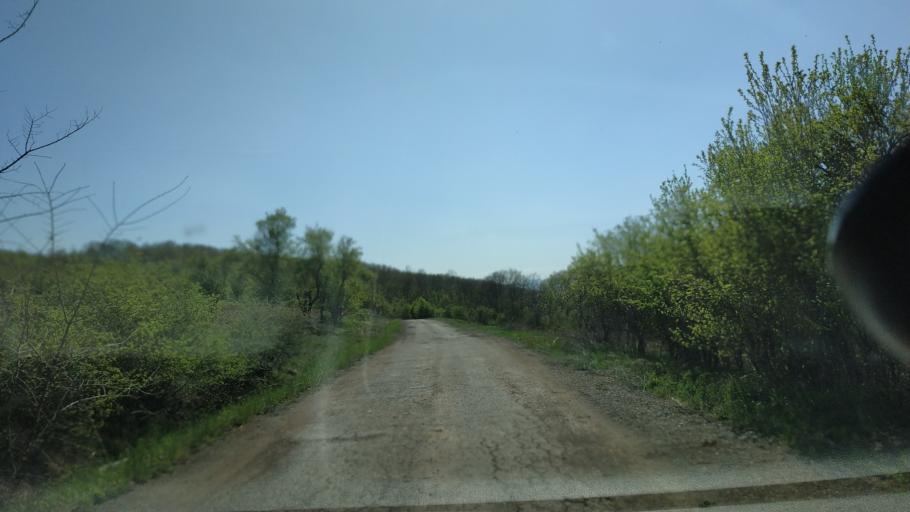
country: RS
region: Central Serbia
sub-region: Zajecarski Okrug
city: Soko Banja
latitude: 43.5100
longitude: 21.9016
